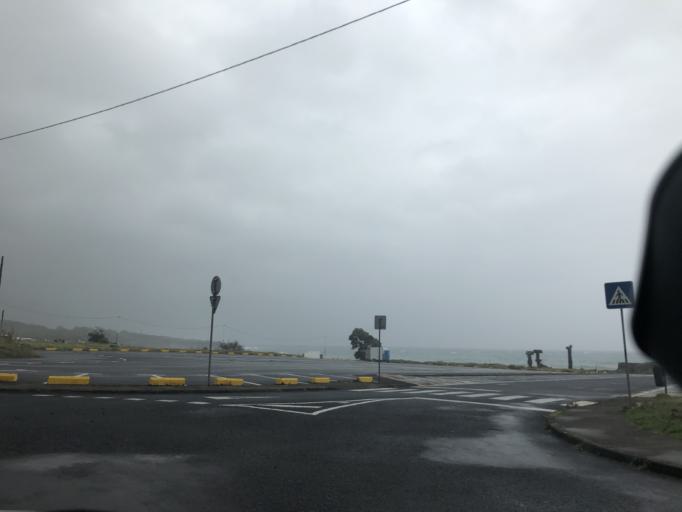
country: PT
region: Azores
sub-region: Ponta Delgada
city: Rosto de Cao
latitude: 37.7506
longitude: -25.6222
